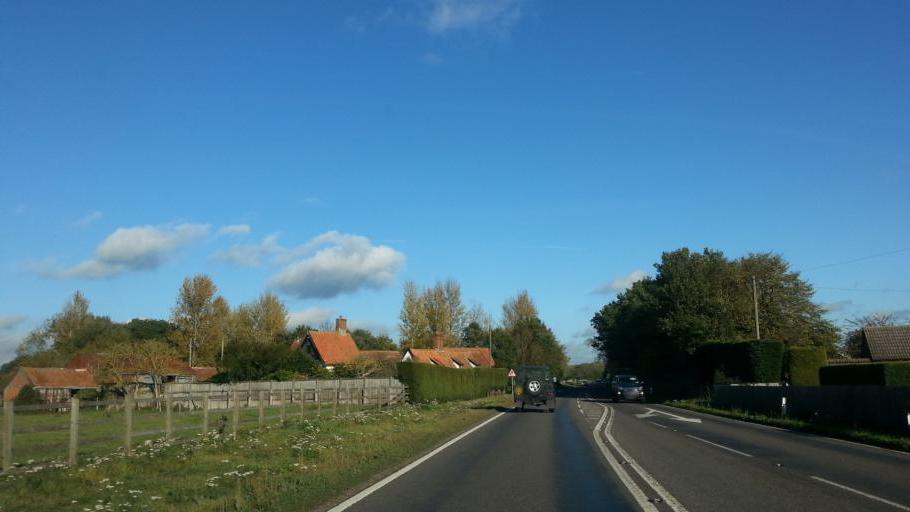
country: GB
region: England
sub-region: Suffolk
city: Bungay
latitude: 52.4515
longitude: 1.4143
